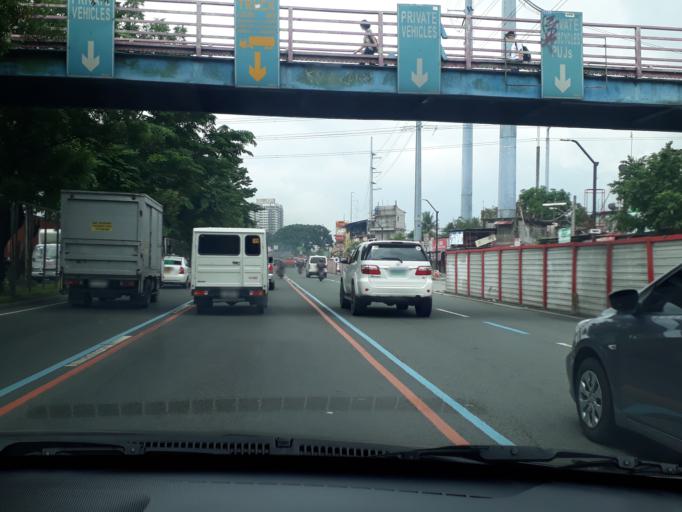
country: PH
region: Calabarzon
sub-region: Province of Rizal
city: Pateros
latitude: 14.5360
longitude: 121.0575
